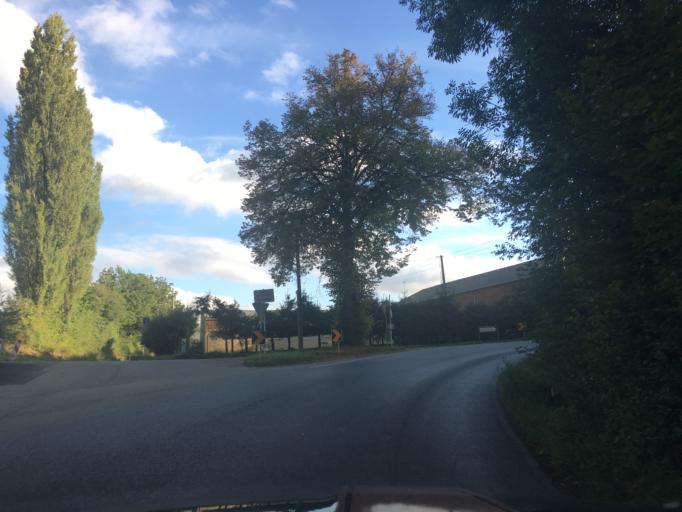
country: FR
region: Lorraine
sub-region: Departement de Meurthe-et-Moselle
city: Hussigny-Godbrange
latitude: 49.5103
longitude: 5.8724
